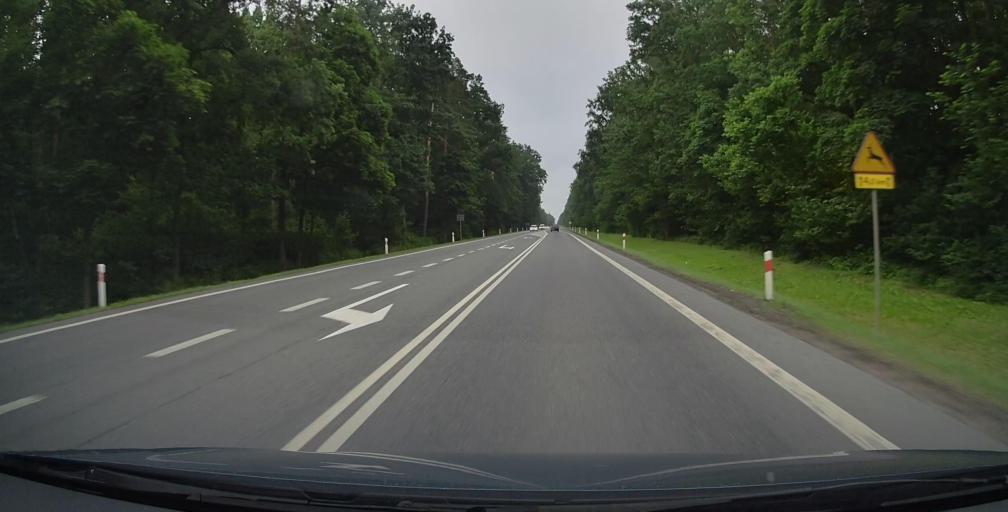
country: PL
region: Lublin Voivodeship
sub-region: Powiat bialski
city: Zalesie
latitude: 52.0359
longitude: 23.3941
